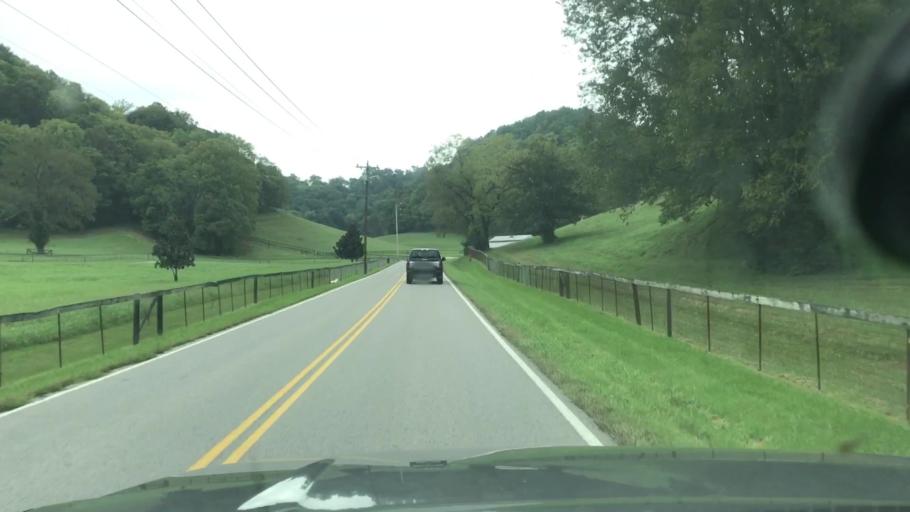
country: US
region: Tennessee
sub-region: Williamson County
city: Brentwood Estates
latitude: 35.9988
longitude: -86.8293
